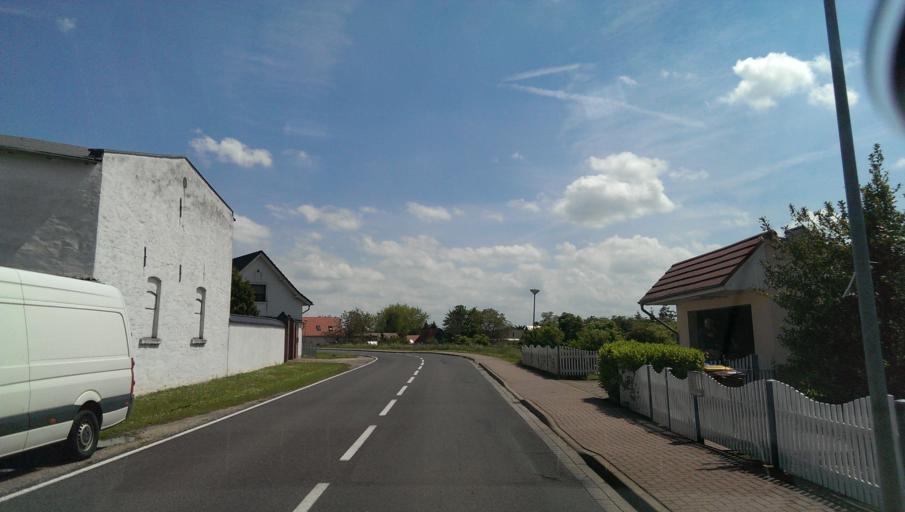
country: DE
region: Saxony-Anhalt
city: Borne
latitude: 51.9501
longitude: 11.5609
